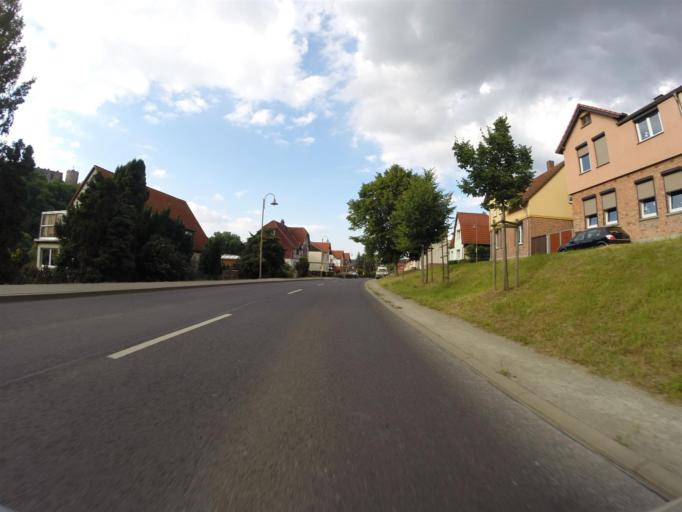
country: DE
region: Thuringia
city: Kranichfeld
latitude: 50.8482
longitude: 11.1949
